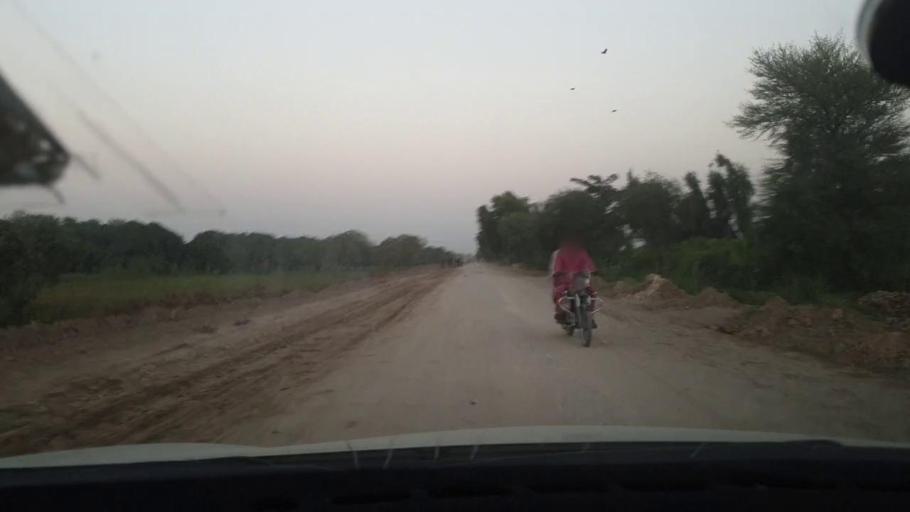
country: PK
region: Sindh
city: Tando Adam
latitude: 25.7532
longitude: 68.5851
